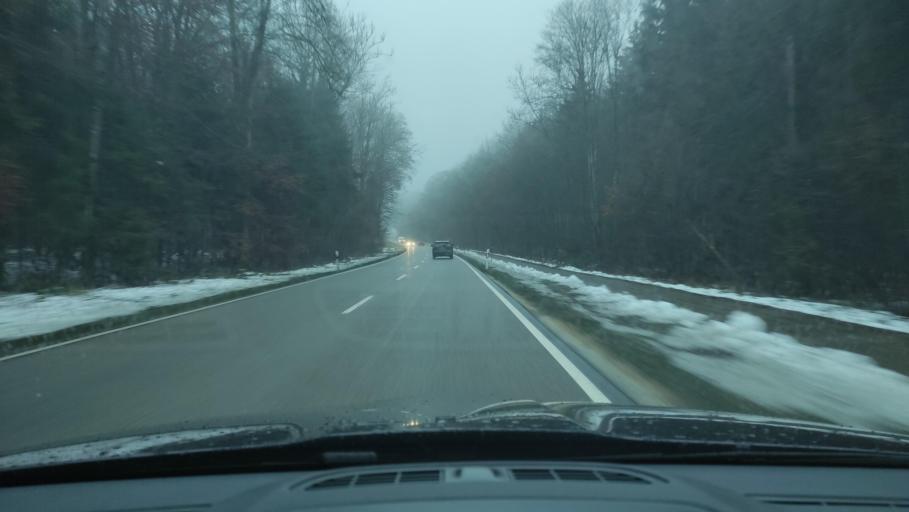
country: DE
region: Bavaria
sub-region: Swabia
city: Weissenhorn
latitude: 48.2925
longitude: 10.1848
